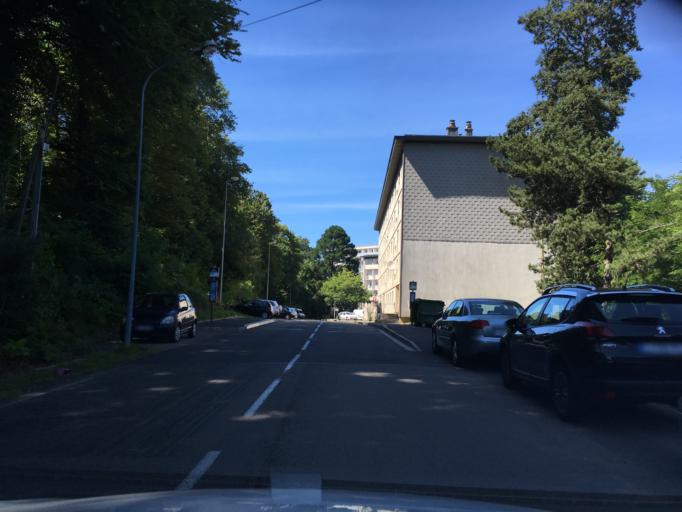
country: FR
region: Brittany
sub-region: Departement du Finistere
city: Quimper
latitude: 47.9836
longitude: -4.1306
